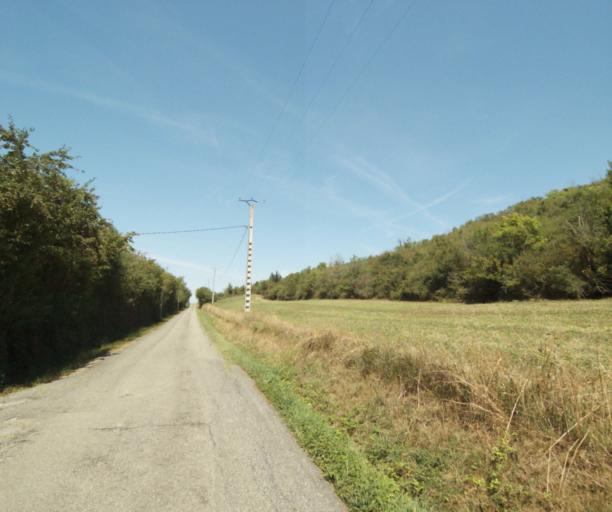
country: FR
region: Midi-Pyrenees
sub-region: Departement de la Haute-Garonne
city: Saint-Sulpice-sur-Leze
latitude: 43.3110
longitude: 1.3396
